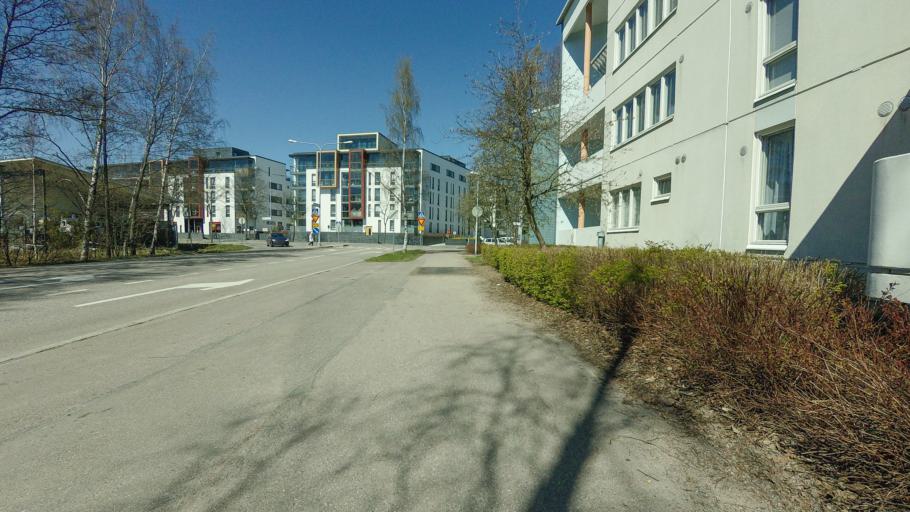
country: FI
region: Uusimaa
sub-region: Helsinki
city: Vantaa
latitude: 60.1921
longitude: 25.0448
